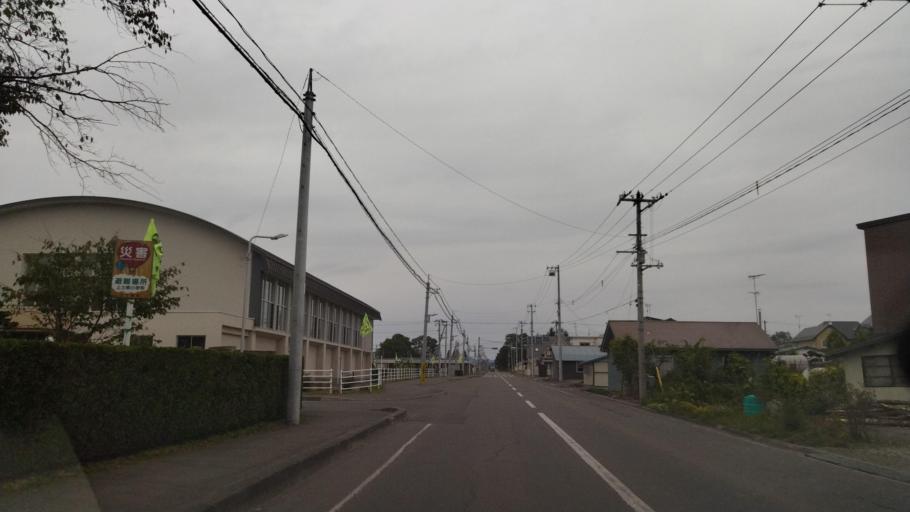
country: JP
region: Hokkaido
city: Otofuke
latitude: 43.2303
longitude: 143.2806
